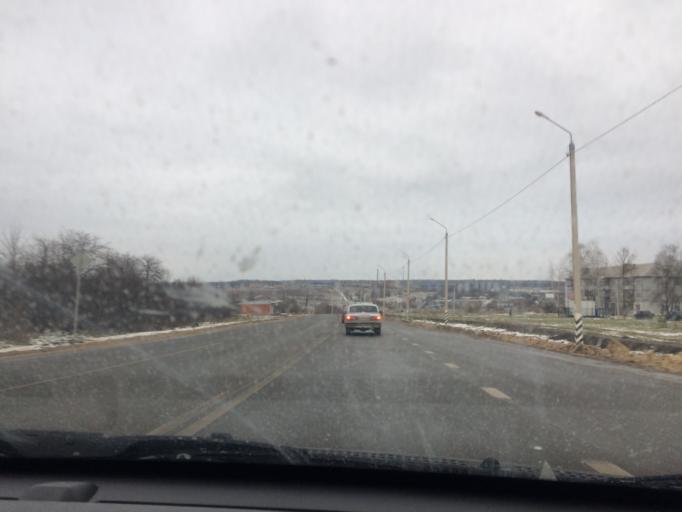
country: RU
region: Tula
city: Gorelki
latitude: 54.2535
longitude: 37.6948
